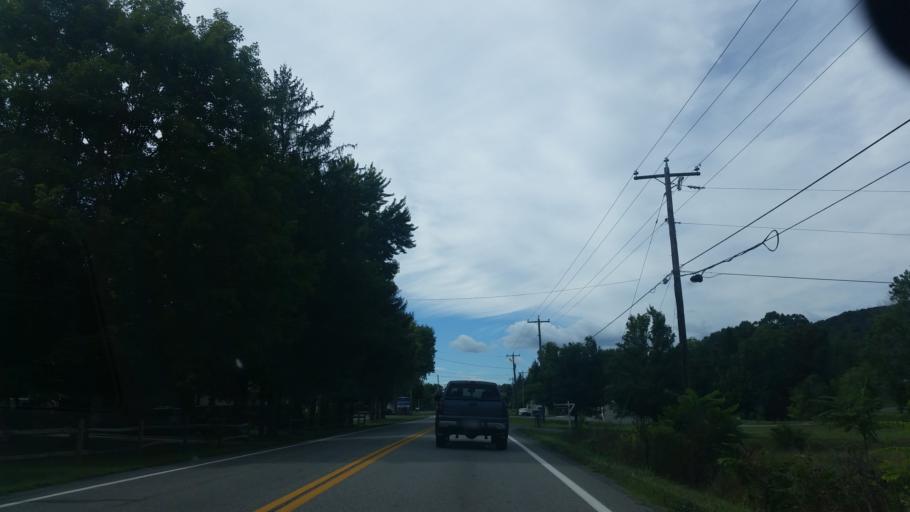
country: US
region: West Virginia
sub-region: Morgan County
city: Berkeley Springs
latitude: 39.6003
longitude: -78.2414
